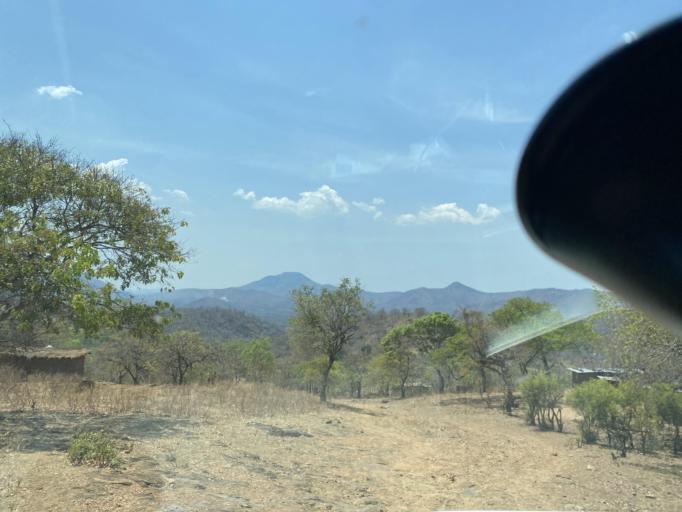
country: ZM
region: Lusaka
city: Kafue
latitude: -15.7958
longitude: 28.4561
